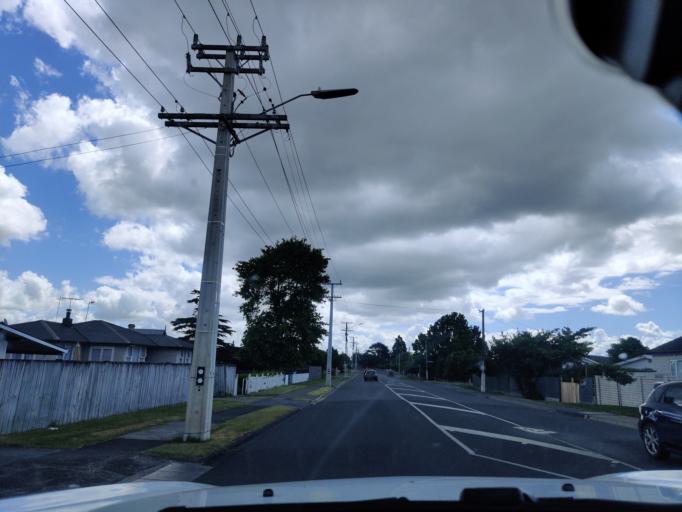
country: NZ
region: Auckland
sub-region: Auckland
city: Red Hill
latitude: -37.0536
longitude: 174.9636
